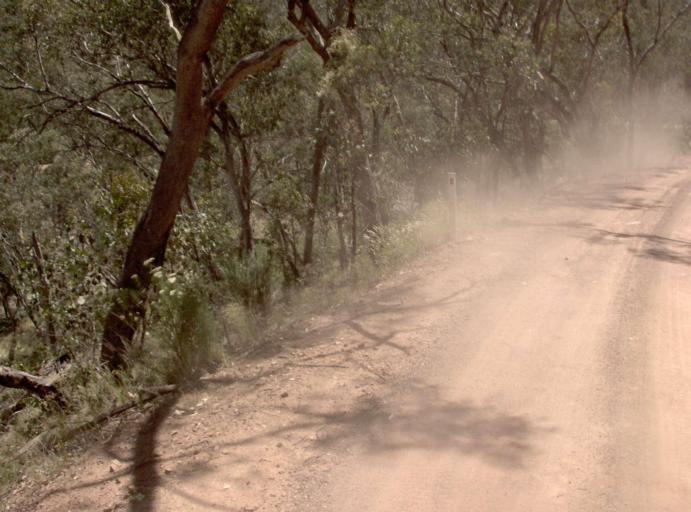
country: AU
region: New South Wales
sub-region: Snowy River
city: Jindabyne
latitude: -37.0871
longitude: 148.3860
